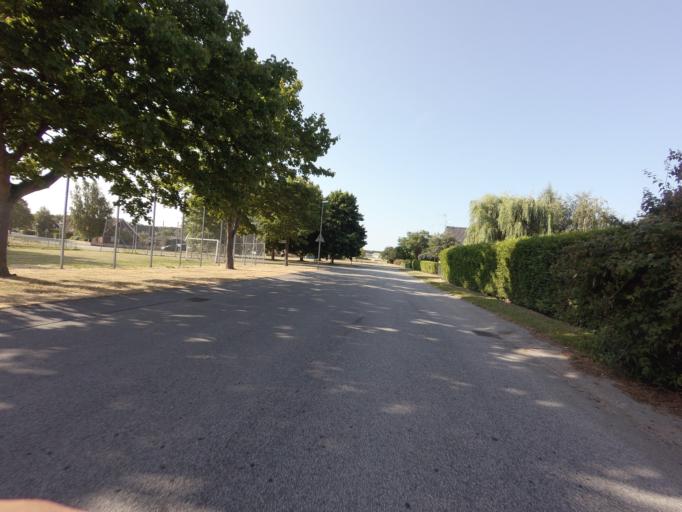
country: SE
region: Skane
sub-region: Landskrona
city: Asmundtorp
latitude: 55.8495
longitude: 12.9227
